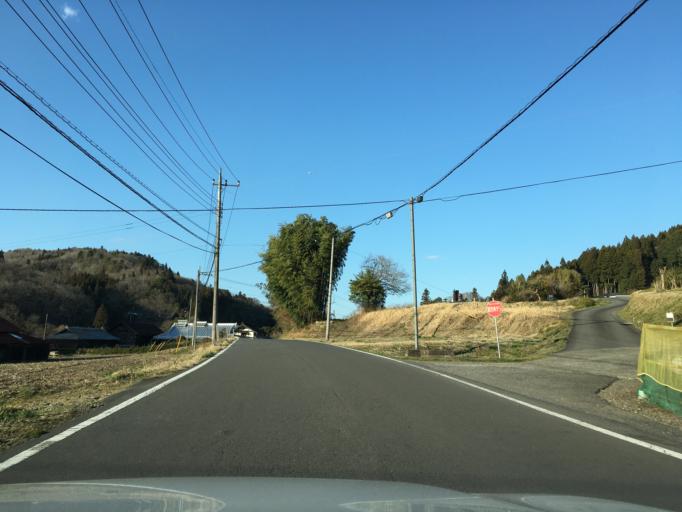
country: JP
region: Tochigi
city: Karasuyama
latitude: 36.7631
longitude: 140.2028
